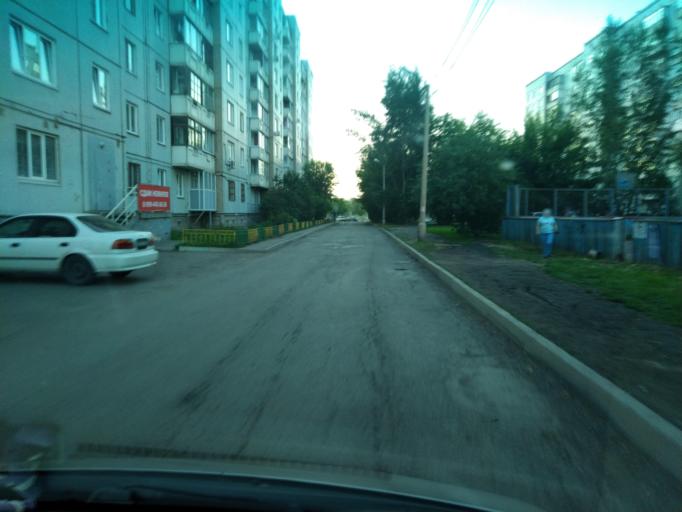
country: RU
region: Krasnoyarskiy
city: Krasnoyarsk
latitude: 55.9862
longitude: 92.8704
